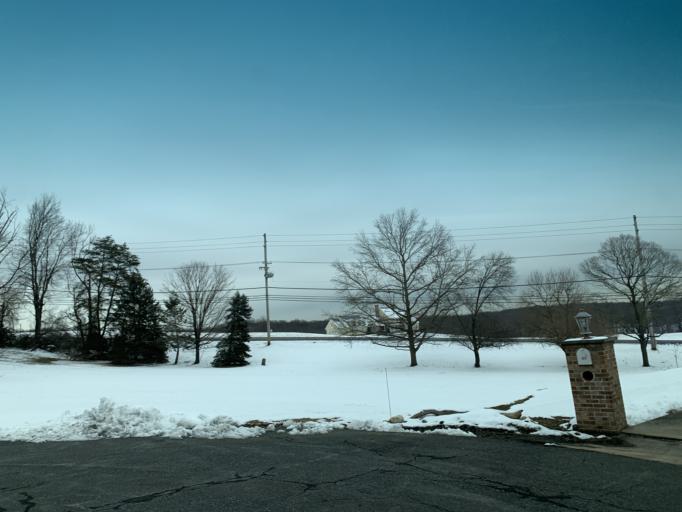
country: US
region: Maryland
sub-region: Harford County
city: Aberdeen
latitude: 39.5601
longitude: -76.1688
